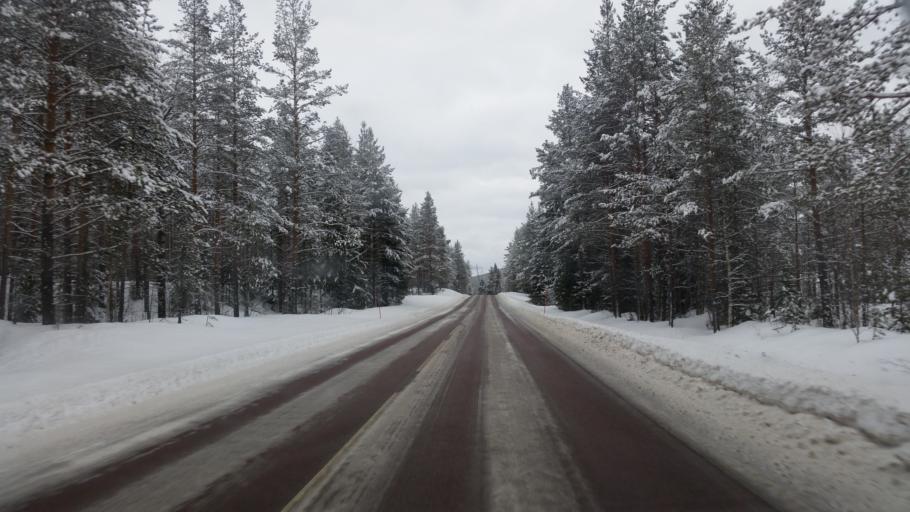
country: SE
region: Jaemtland
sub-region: Bergs Kommun
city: Hoverberg
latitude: 62.4078
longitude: 14.6241
